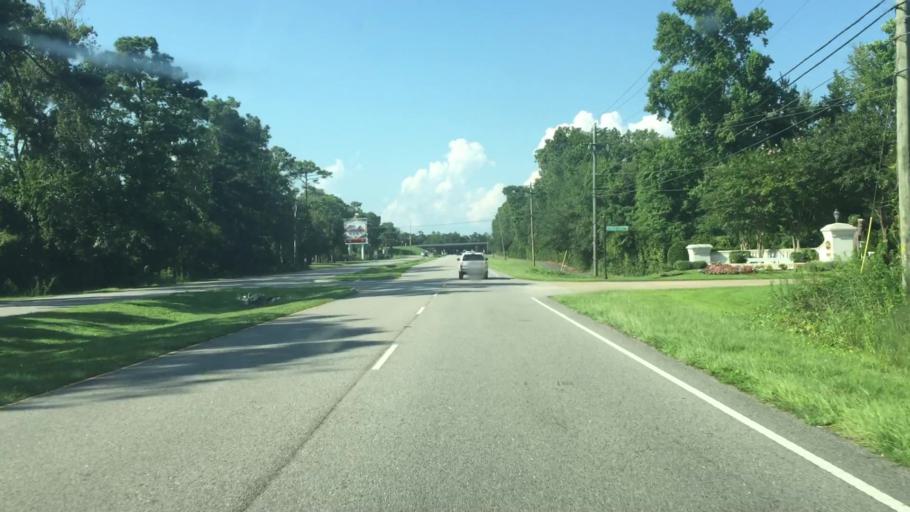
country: US
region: South Carolina
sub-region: Horry County
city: Myrtle Beach
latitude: 33.7623
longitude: -78.8062
